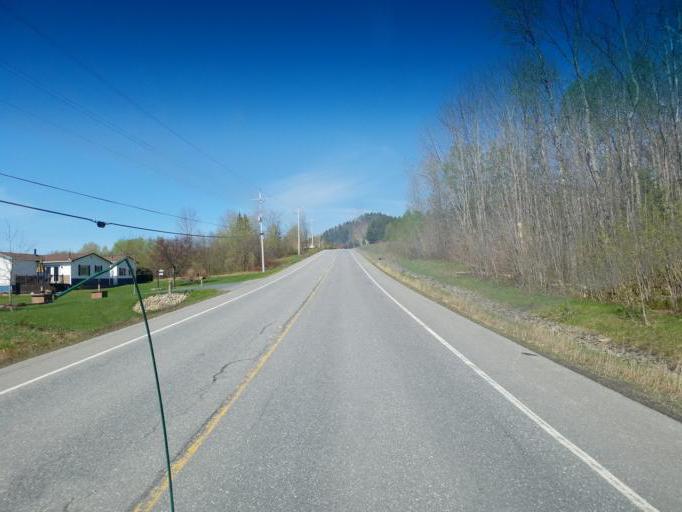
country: US
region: Maine
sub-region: Aroostook County
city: Presque Isle
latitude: 46.6666
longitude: -68.2174
